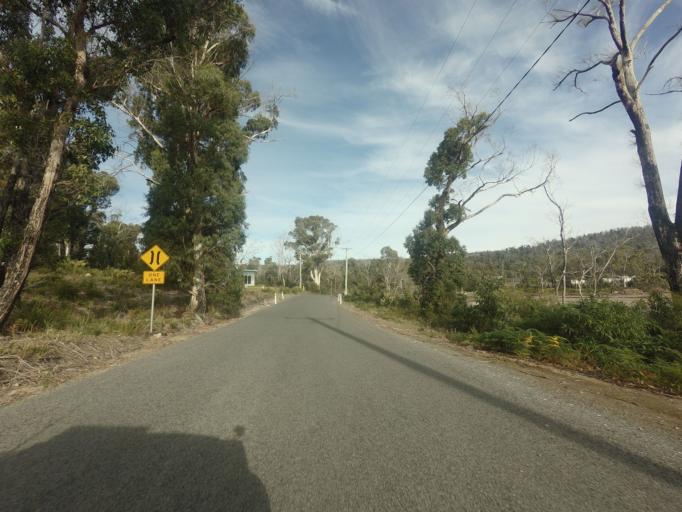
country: AU
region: Tasmania
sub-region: Sorell
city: Sorell
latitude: -42.9563
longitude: 147.8534
